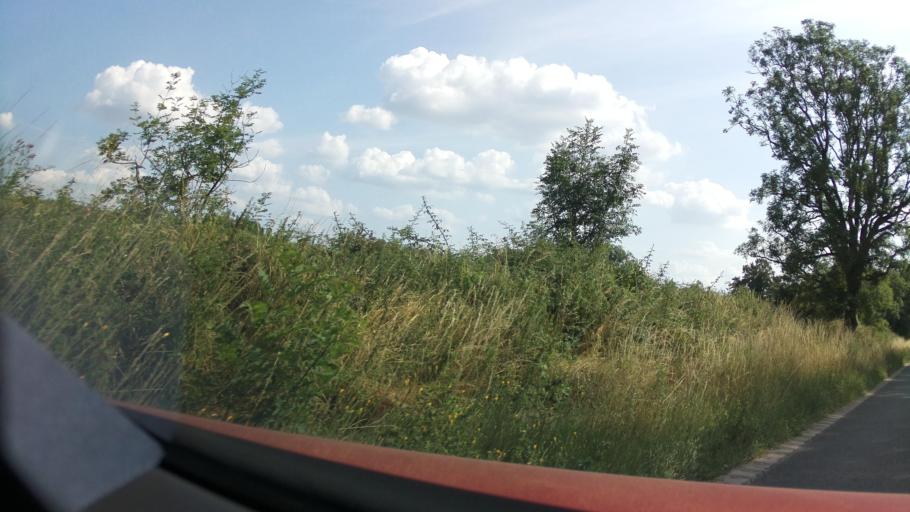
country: GB
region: England
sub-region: Wiltshire
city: Leigh
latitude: 51.6634
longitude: -1.9109
